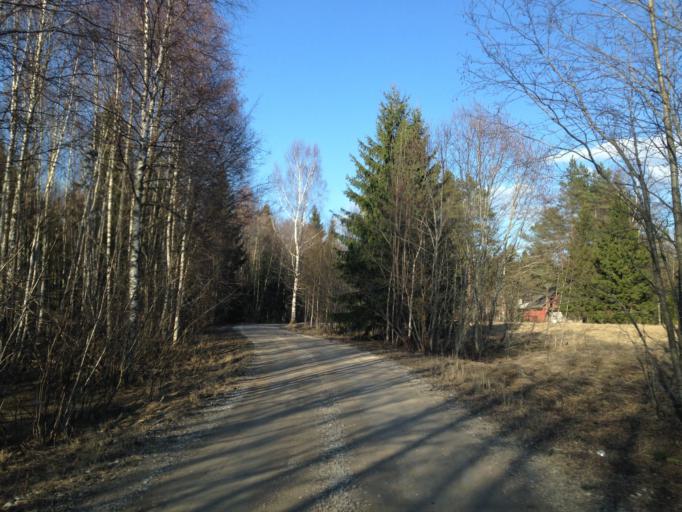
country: EE
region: Harju
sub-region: Nissi vald
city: Turba
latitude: 59.1338
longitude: 24.1690
